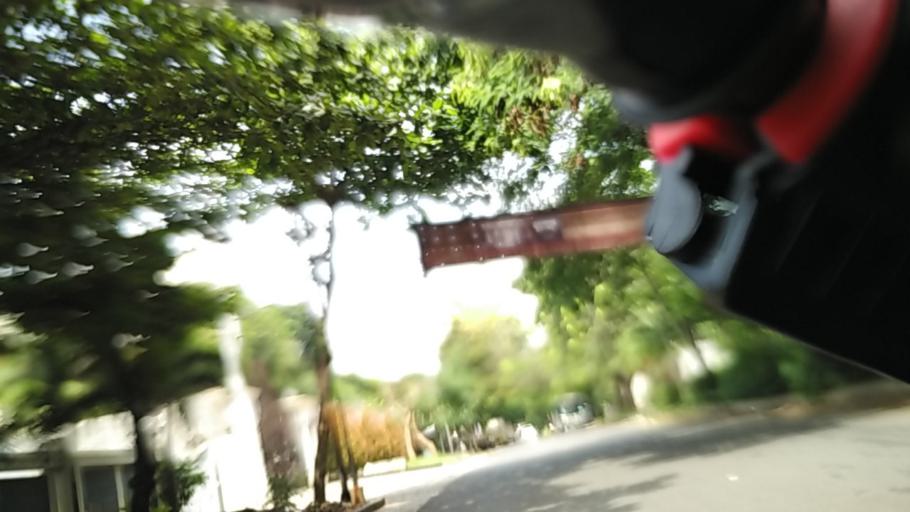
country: ID
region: Central Java
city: Semarang
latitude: -7.0093
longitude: 110.4244
